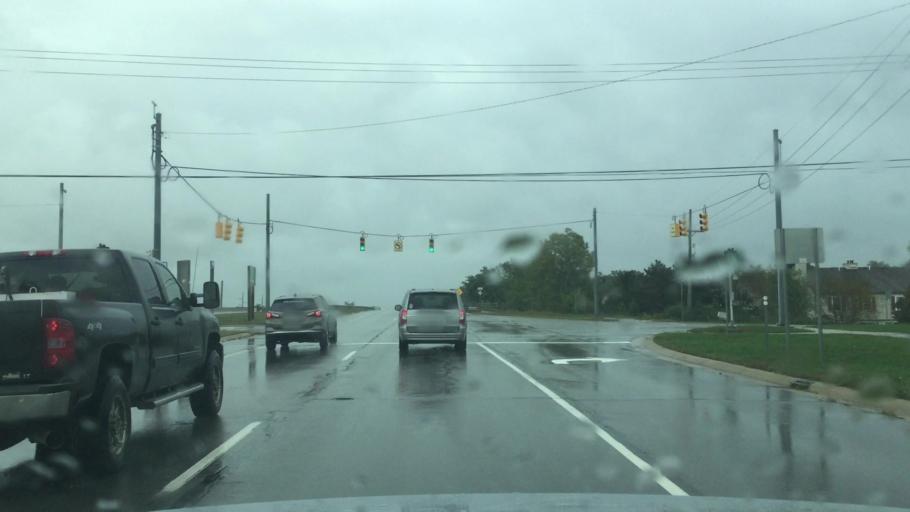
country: US
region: Michigan
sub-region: Livingston County
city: Howell
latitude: 42.6216
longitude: -83.9423
